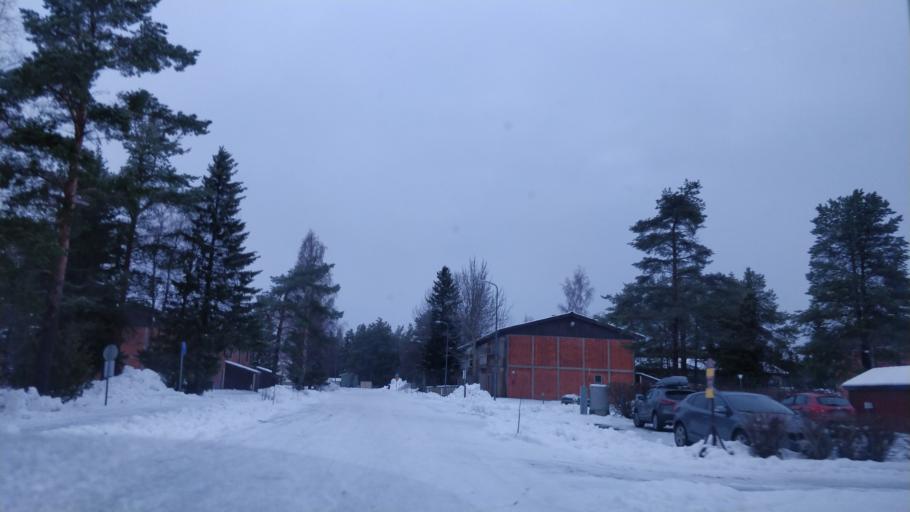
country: FI
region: Lapland
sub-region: Kemi-Tornio
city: Kemi
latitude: 65.7419
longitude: 24.6012
